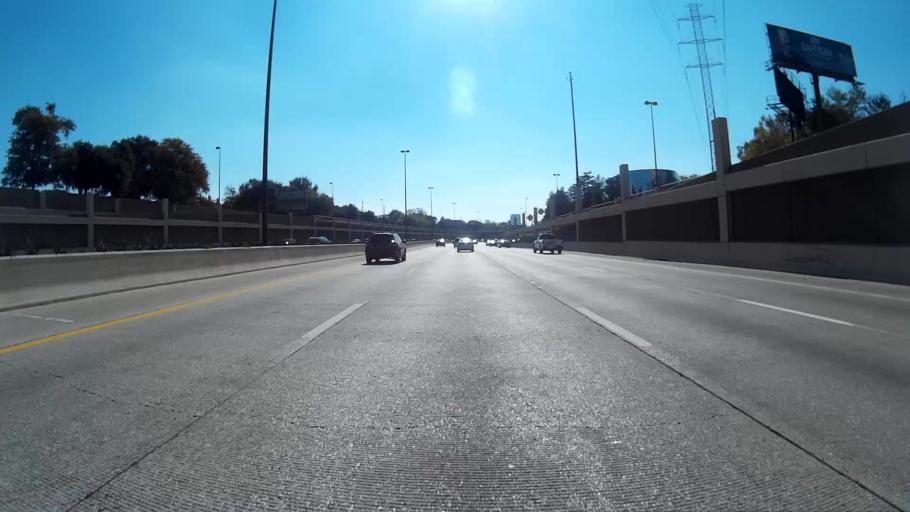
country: US
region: Texas
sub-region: Dallas County
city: Highland Park
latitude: 32.8332
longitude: -96.7804
